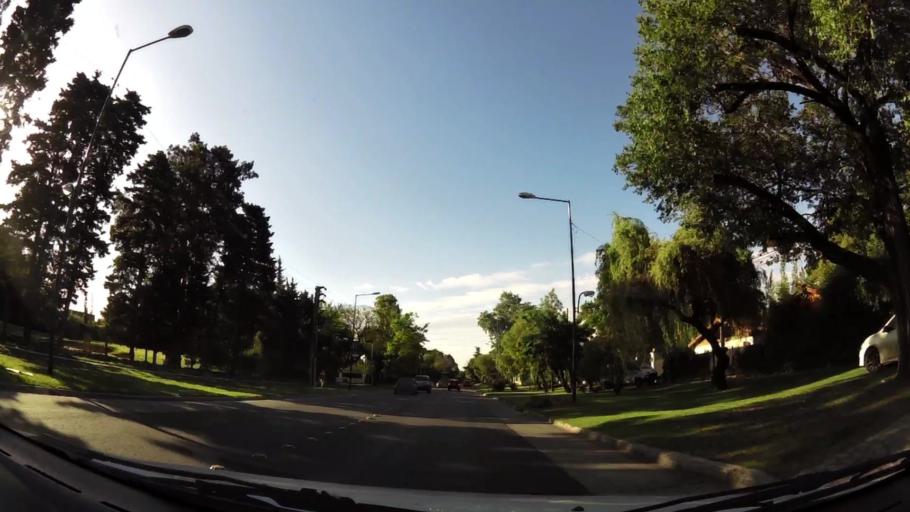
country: AR
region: Buenos Aires
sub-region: Partido de San Isidro
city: San Isidro
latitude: -34.4858
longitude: -58.5503
